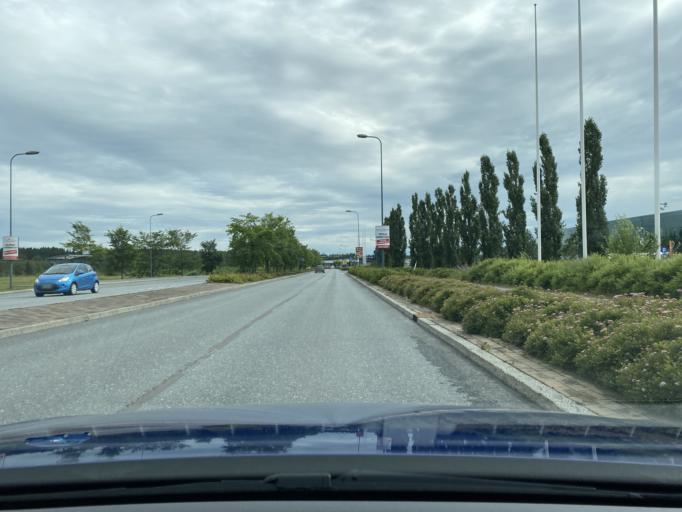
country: FI
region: Pirkanmaa
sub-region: Tampere
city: Lempaeaelae
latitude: 61.3629
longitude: 23.7986
